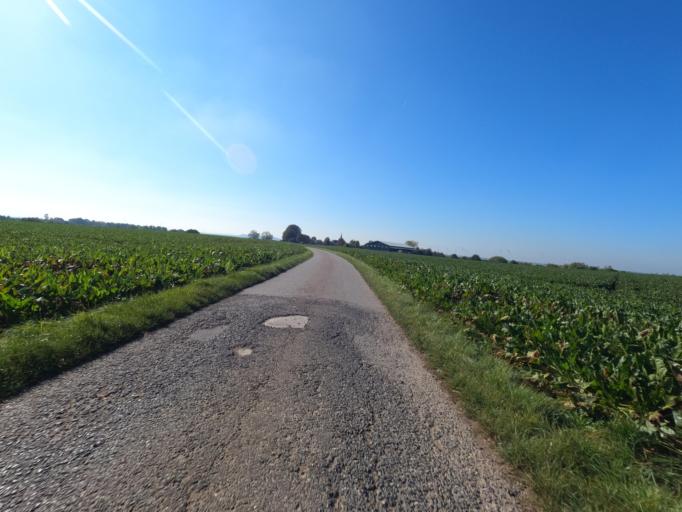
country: DE
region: North Rhine-Westphalia
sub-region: Regierungsbezirk Koln
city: Linnich
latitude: 50.9991
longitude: 6.2985
